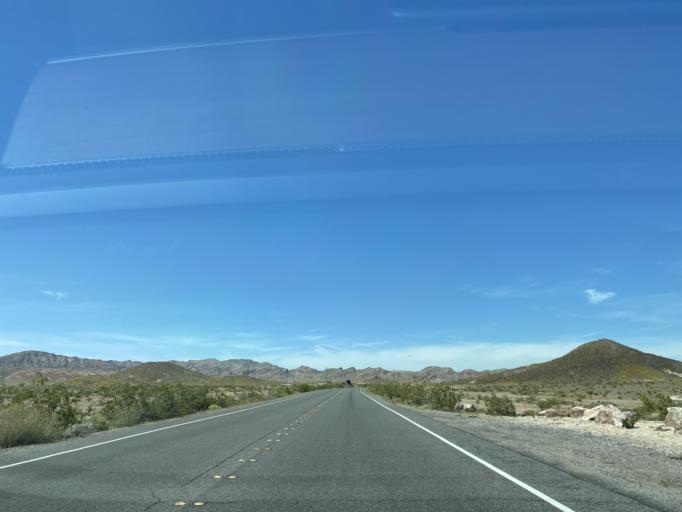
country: US
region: Nevada
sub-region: Clark County
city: Henderson
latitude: 36.1655
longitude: -114.9096
